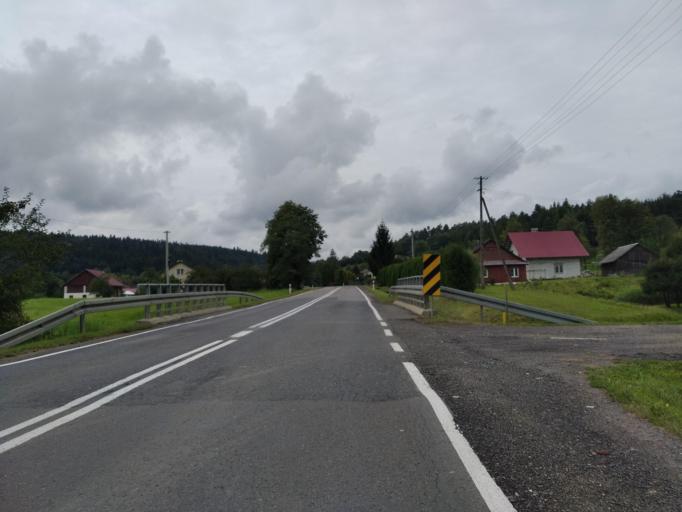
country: PL
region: Subcarpathian Voivodeship
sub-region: Powiat przemyski
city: Bircza
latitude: 49.6903
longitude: 22.4461
